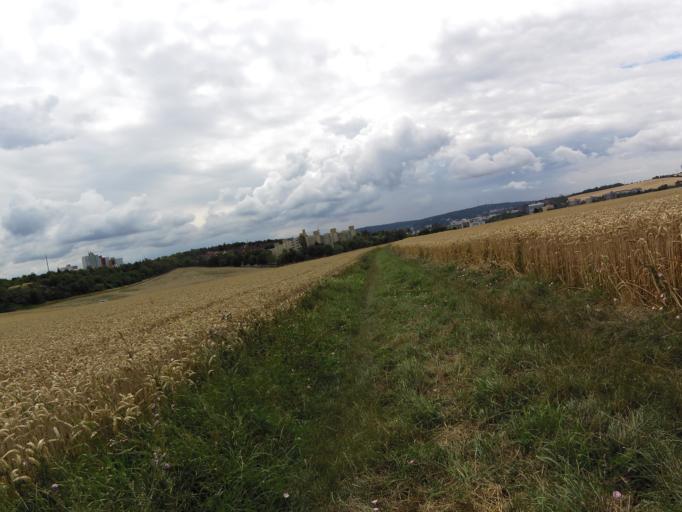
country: DE
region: Bavaria
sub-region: Regierungsbezirk Unterfranken
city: Estenfeld
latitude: 49.8176
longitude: 9.9777
